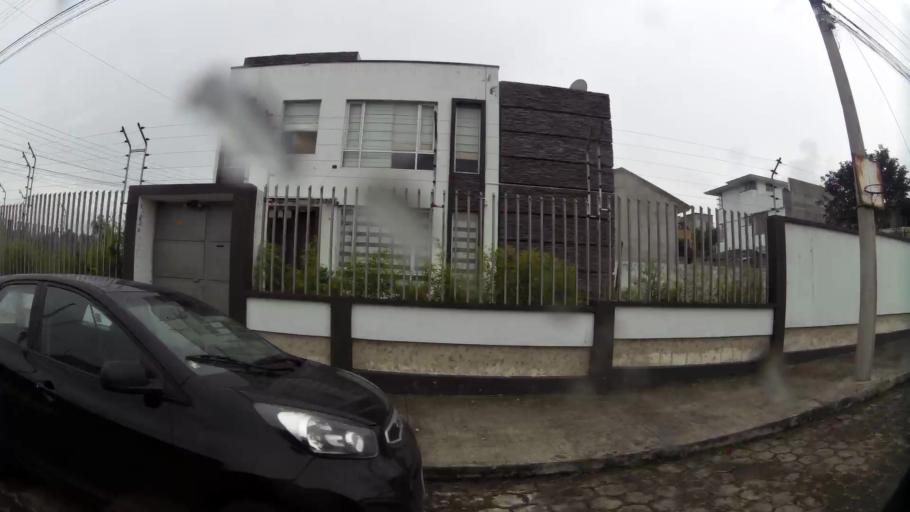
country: EC
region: Pichincha
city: Sangolqui
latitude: -0.3223
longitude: -78.4314
